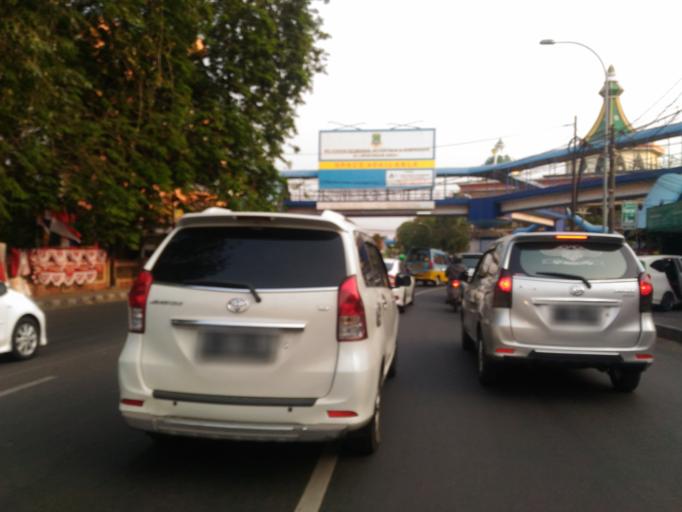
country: ID
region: Banten
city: Tangerang
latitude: -6.1751
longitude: 106.6300
